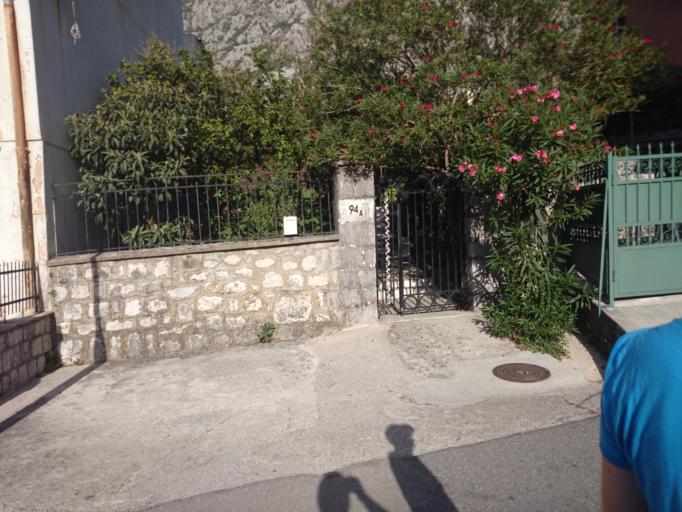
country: ME
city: Dobrota
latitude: 42.4380
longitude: 18.7642
